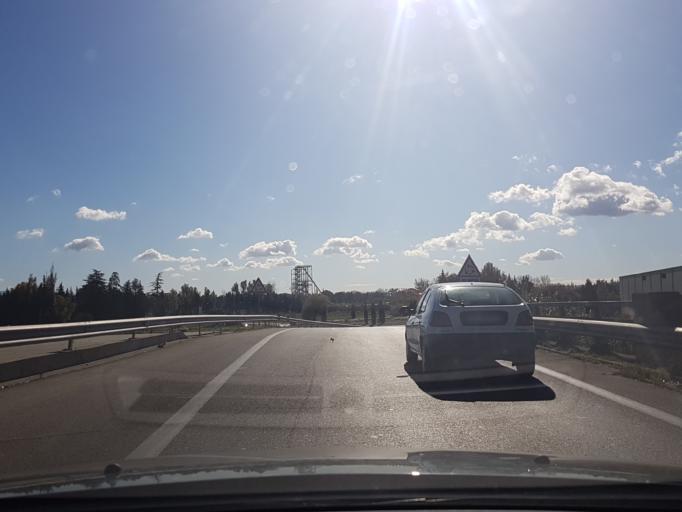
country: FR
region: Provence-Alpes-Cote d'Azur
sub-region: Departement du Vaucluse
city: Althen-des-Paluds
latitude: 44.0290
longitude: 4.9677
